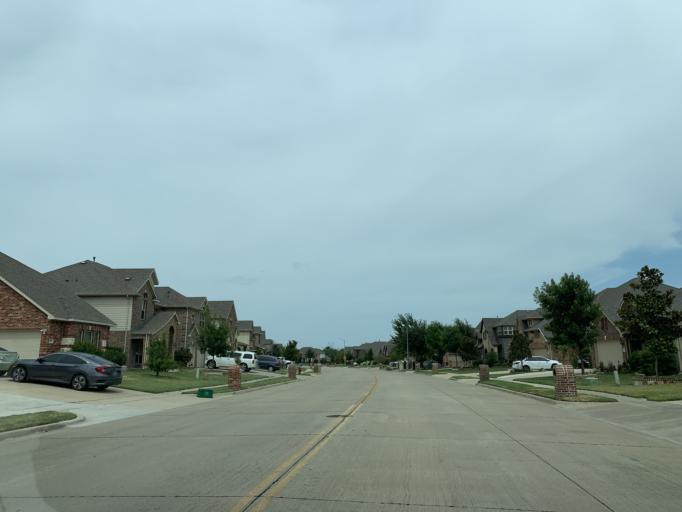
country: US
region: Texas
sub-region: Dallas County
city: Grand Prairie
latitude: 32.6518
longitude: -97.0382
